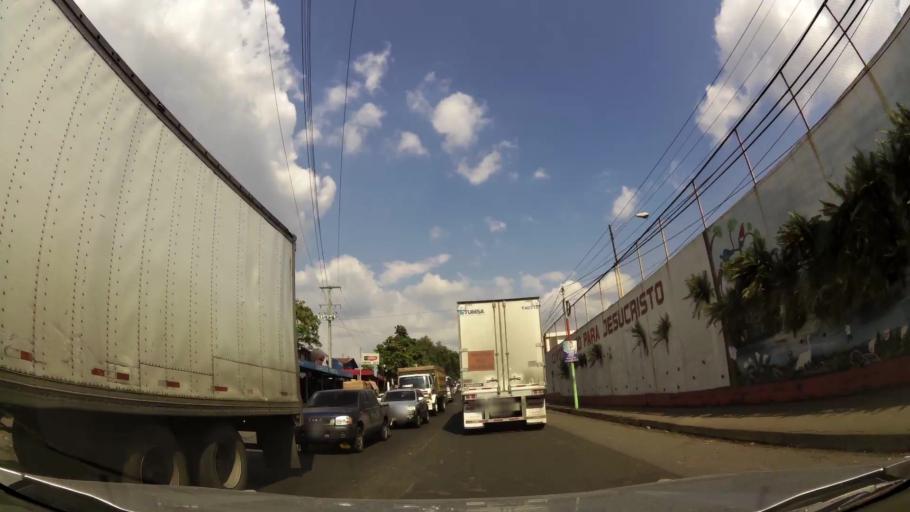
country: GT
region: Suchitepeque
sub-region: Municipio de Cuyotenango
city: Cuyotenango
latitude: 14.5419
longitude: -91.5697
